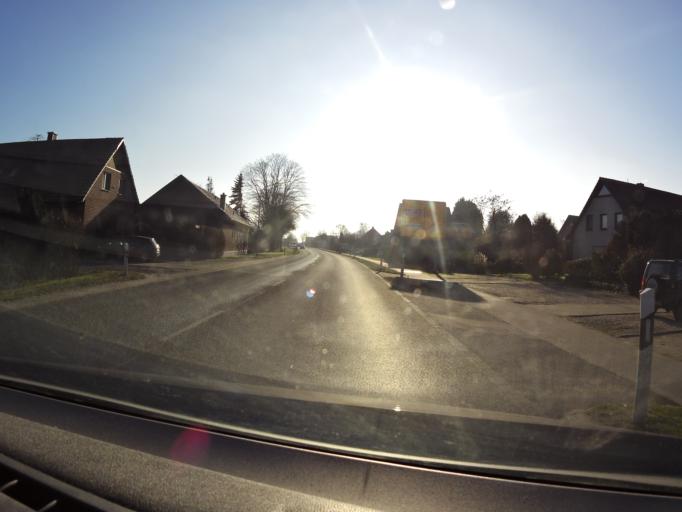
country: DE
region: North Rhine-Westphalia
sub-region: Regierungsbezirk Dusseldorf
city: Bruggen
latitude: 51.2552
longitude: 6.1837
